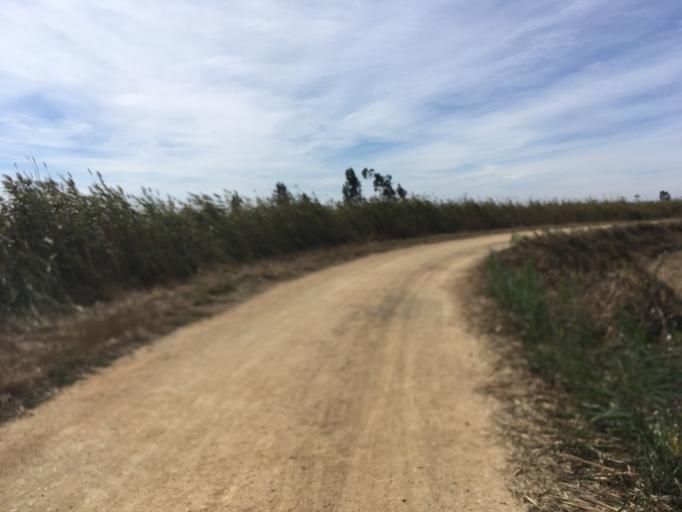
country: PT
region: Aveiro
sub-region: Estarreja
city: Salreu
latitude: 40.7312
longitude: -8.5731
